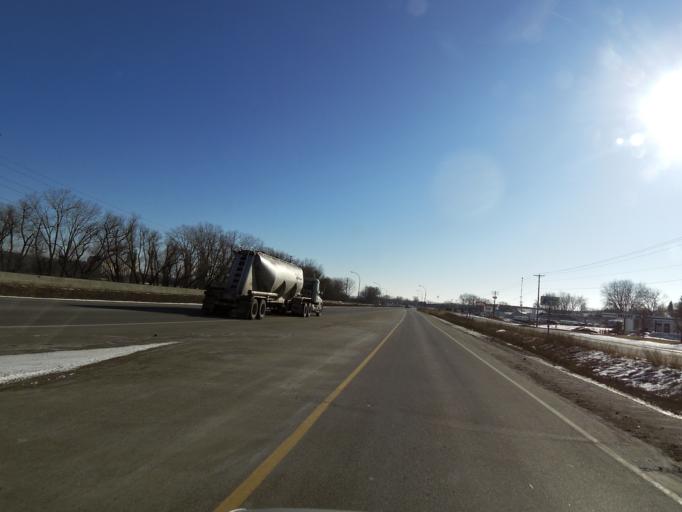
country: US
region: Minnesota
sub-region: Scott County
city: Savage
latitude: 44.7785
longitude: -93.3745
